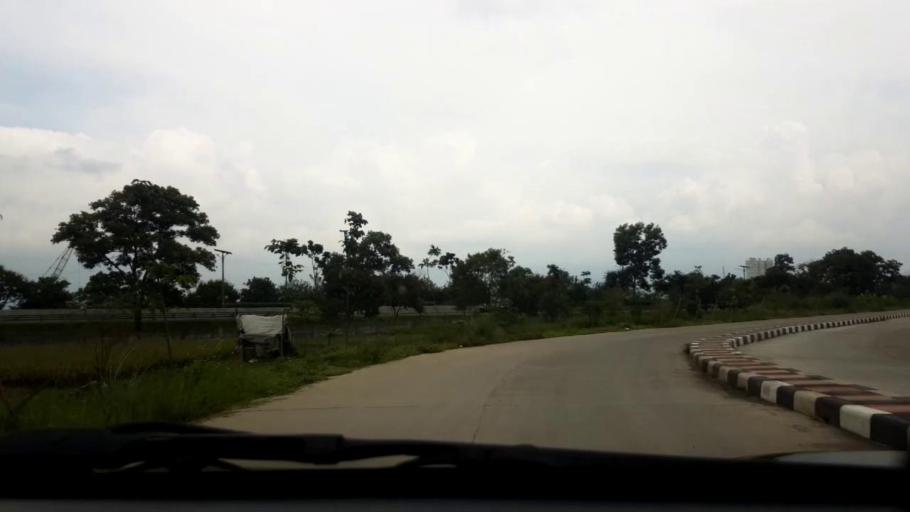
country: ID
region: West Java
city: Cileunyi
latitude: -6.9610
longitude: 107.7155
